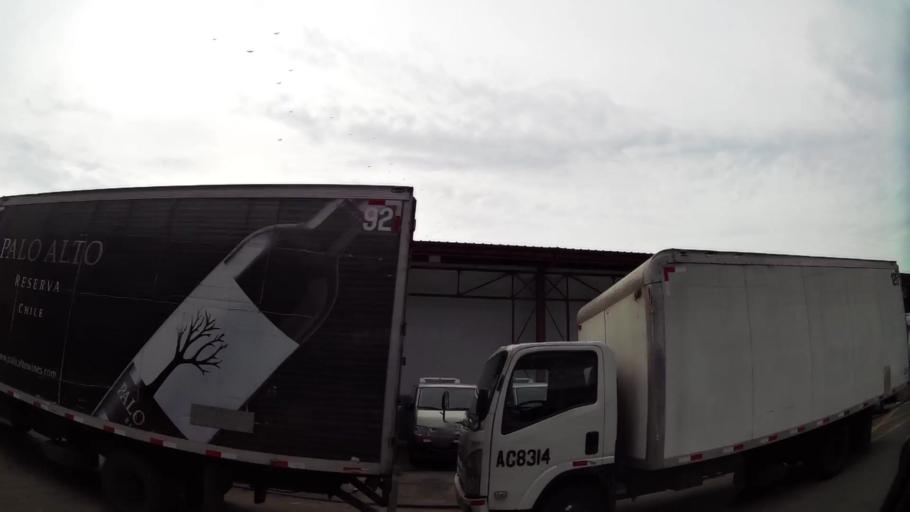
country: PA
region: Panama
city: San Miguelito
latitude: 9.0132
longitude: -79.4821
